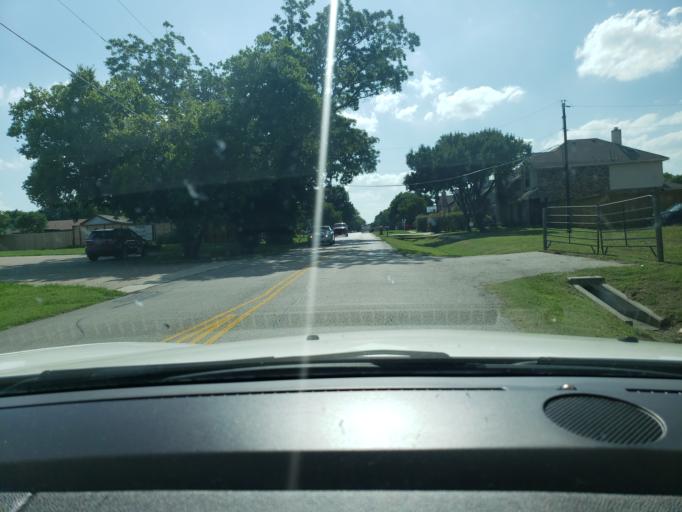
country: US
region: Texas
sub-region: Dallas County
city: Rowlett
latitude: 32.8968
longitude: -96.5711
